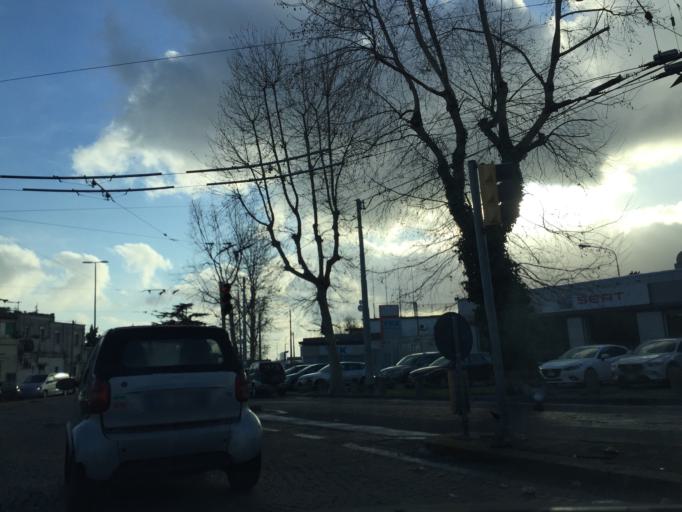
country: IT
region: Campania
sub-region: Provincia di Napoli
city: Casavatore
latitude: 40.8697
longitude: 14.2845
